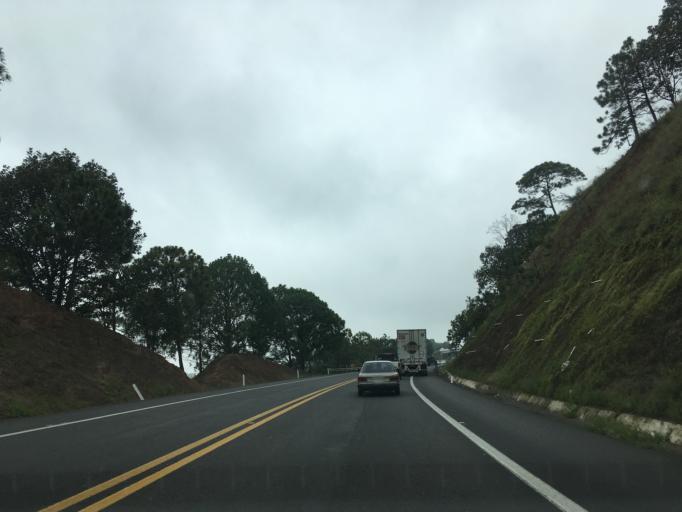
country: MX
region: Michoacan
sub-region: Uruapan
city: Toreo Bajo (El Toreo Bajo)
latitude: 19.4159
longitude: -101.9812
